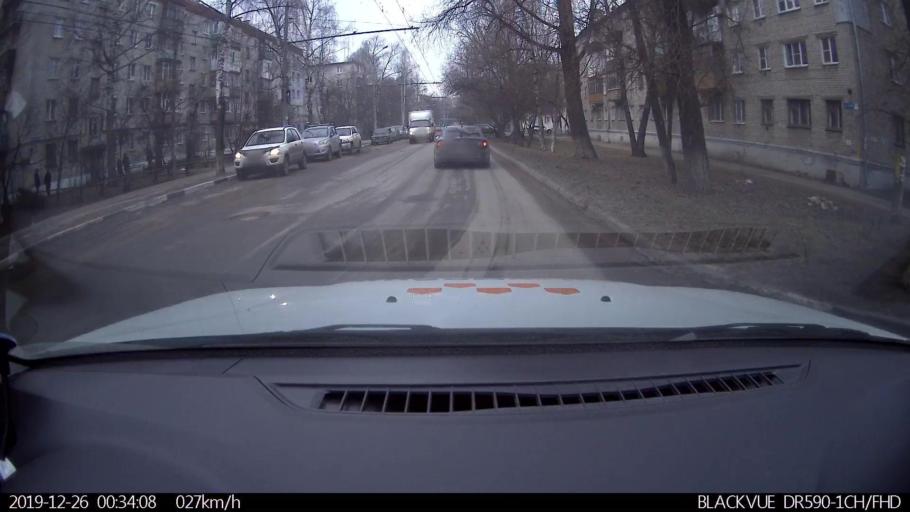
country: RU
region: Nizjnij Novgorod
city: Nizhniy Novgorod
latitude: 56.2891
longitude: 43.9185
